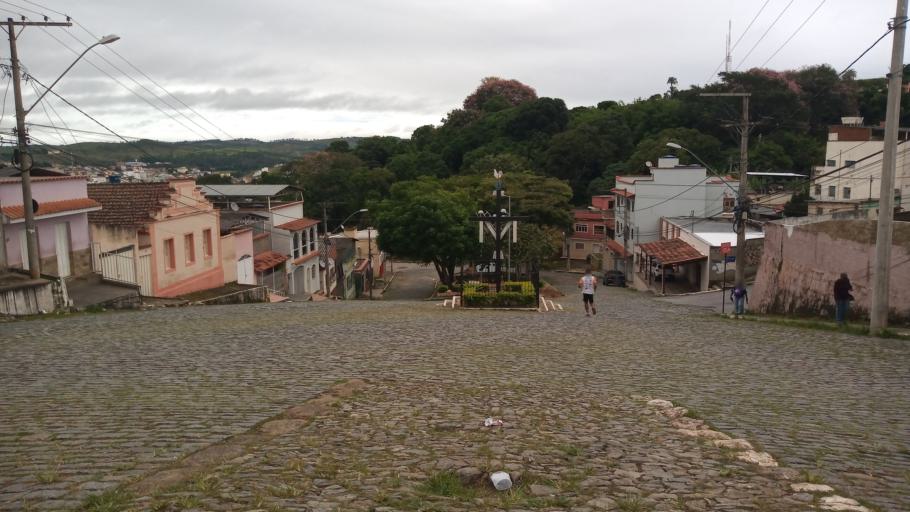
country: BR
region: Minas Gerais
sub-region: Sao Joao Del Rei
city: Sao Joao del Rei
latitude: -21.1275
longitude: -44.2641
